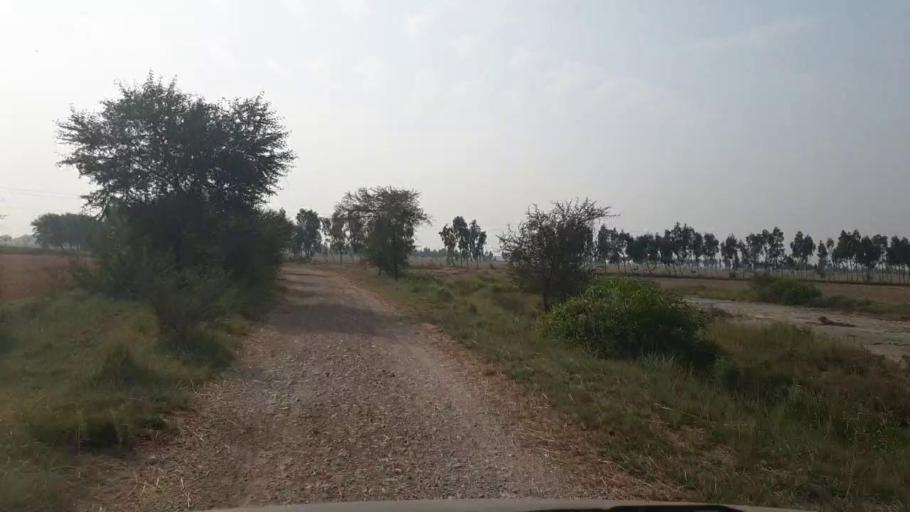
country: PK
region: Sindh
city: Tando Muhammad Khan
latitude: 25.0993
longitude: 68.5023
